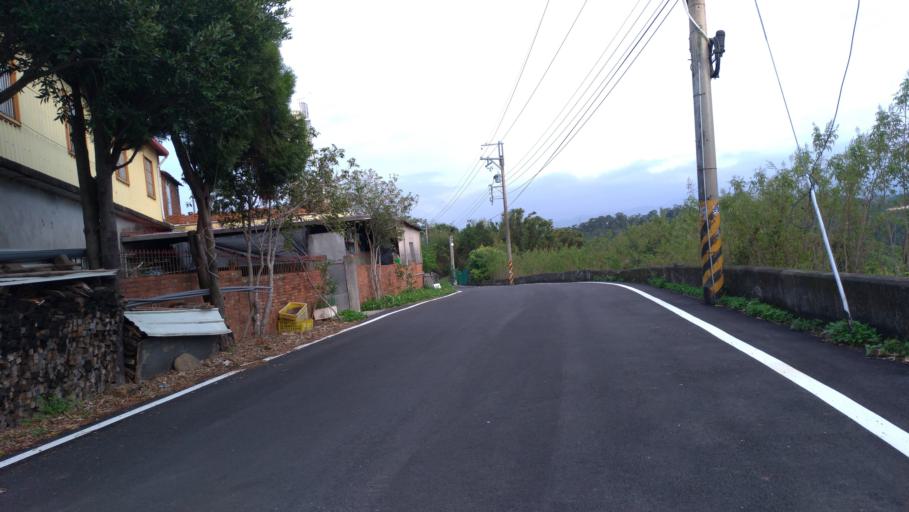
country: TW
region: Taiwan
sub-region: Hsinchu
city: Hsinchu
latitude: 24.7507
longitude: 120.9868
